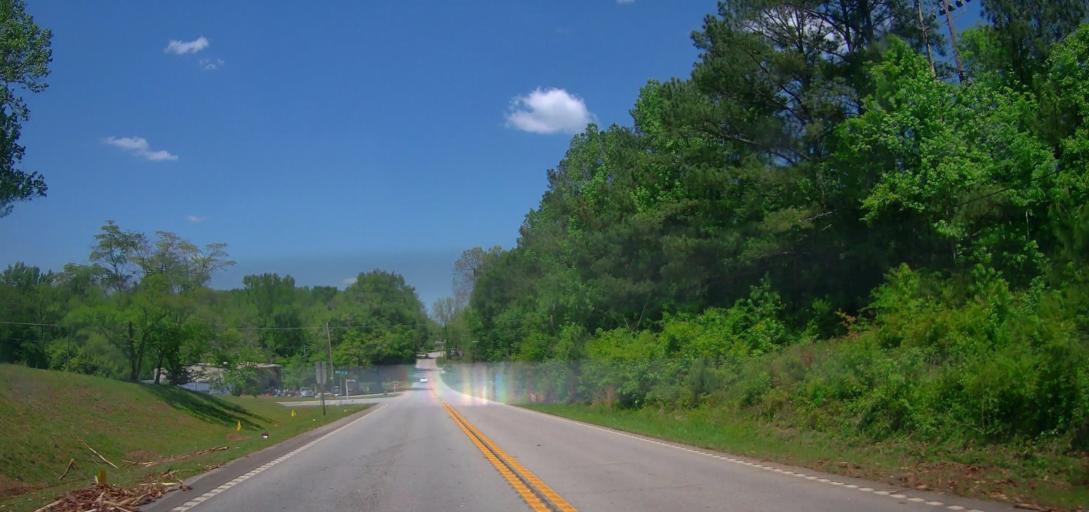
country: US
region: Georgia
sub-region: Jasper County
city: Monticello
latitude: 33.2937
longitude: -83.6797
